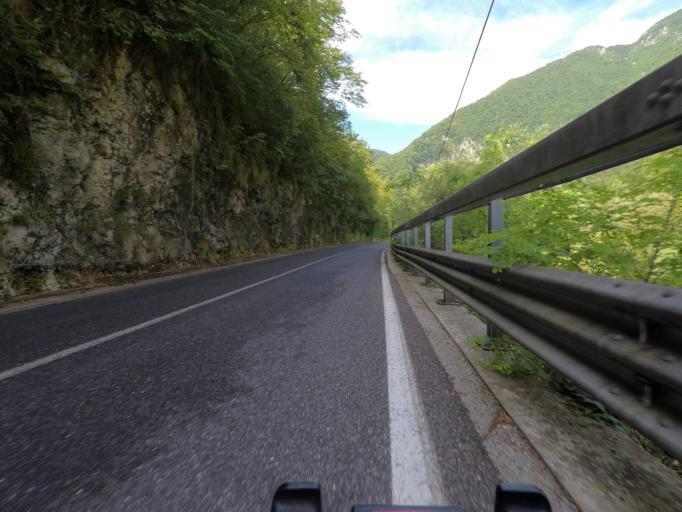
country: IT
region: Friuli Venezia Giulia
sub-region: Provincia di Udine
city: Pulfero
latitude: 46.2042
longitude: 13.4764
